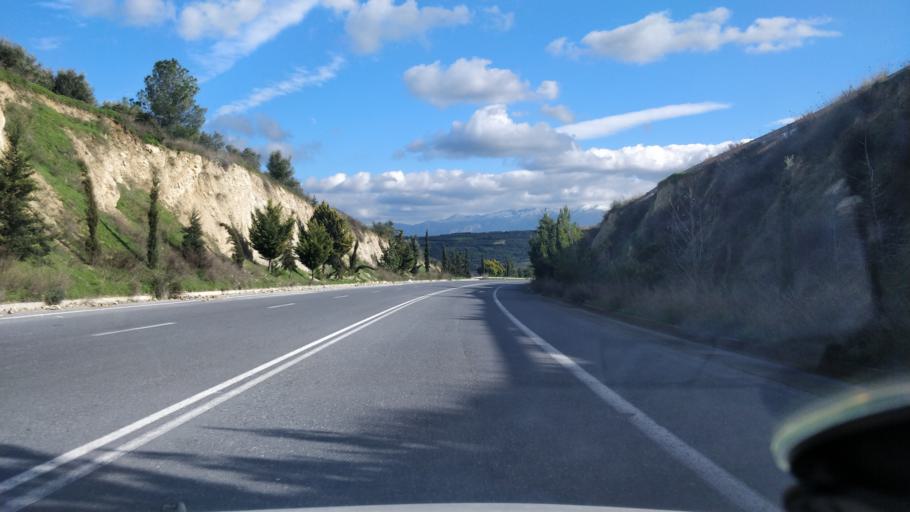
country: GR
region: Crete
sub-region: Nomos Irakleiou
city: Ano Arhanes
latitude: 35.2243
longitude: 25.1904
